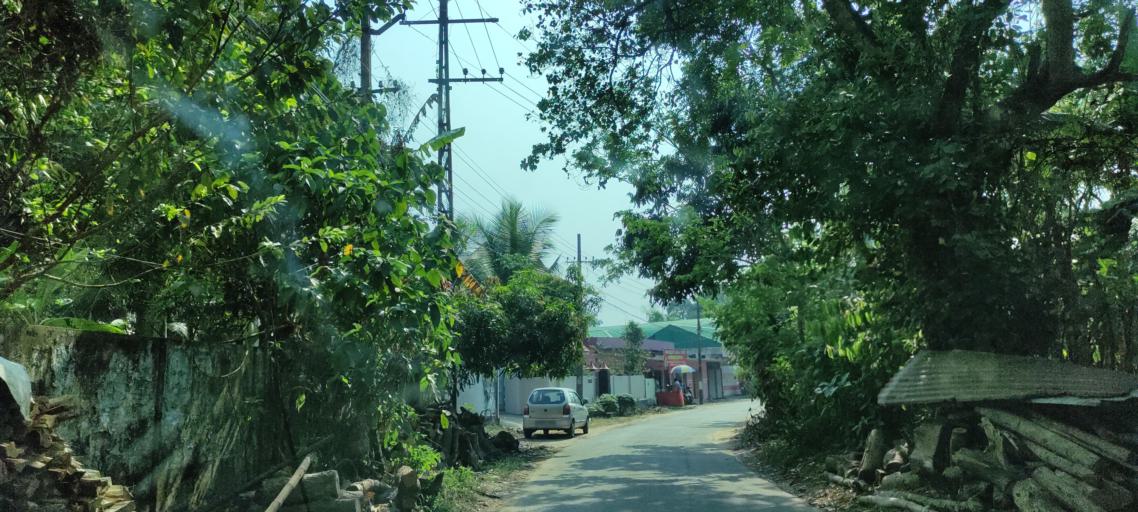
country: IN
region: Kerala
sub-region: Pattanamtitta
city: Tiruvalla
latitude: 9.3550
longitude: 76.5261
